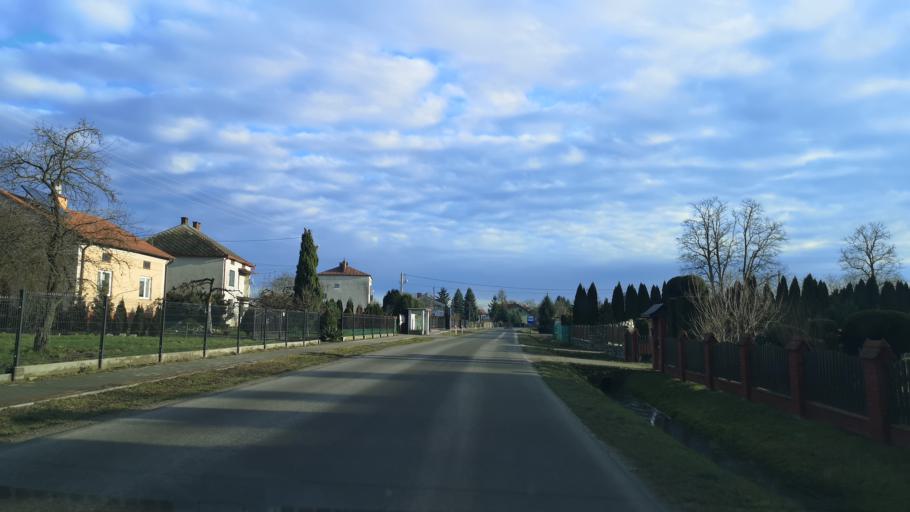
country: PL
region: Subcarpathian Voivodeship
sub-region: Powiat lezajski
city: Piskorowice
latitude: 50.2427
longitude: 22.5153
